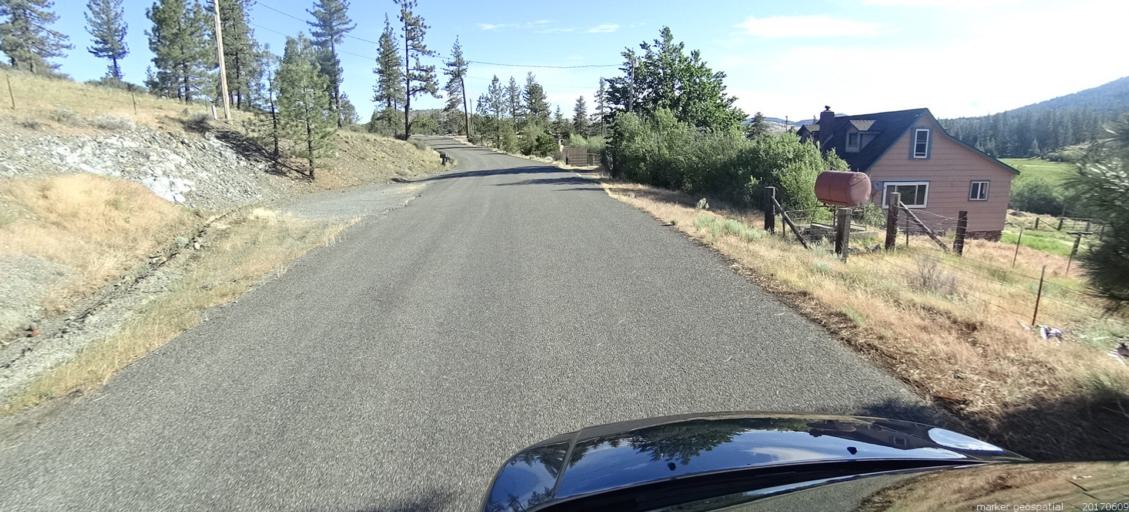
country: US
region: California
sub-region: Siskiyou County
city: Weed
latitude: 41.3480
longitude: -122.7236
